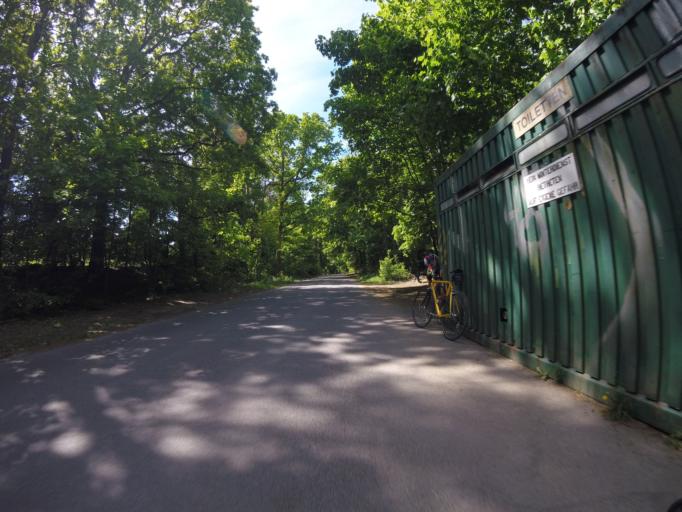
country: DE
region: Berlin
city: Grunewald
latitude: 52.4681
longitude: 13.2343
